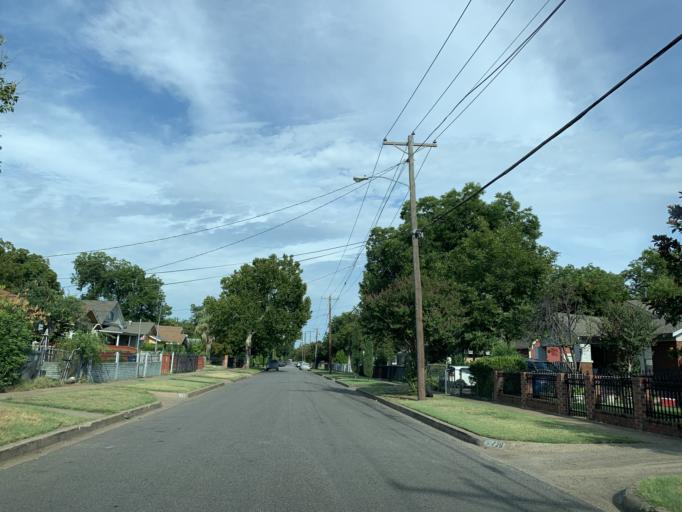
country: US
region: Texas
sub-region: Dallas County
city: Dallas
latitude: 32.7402
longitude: -96.8355
